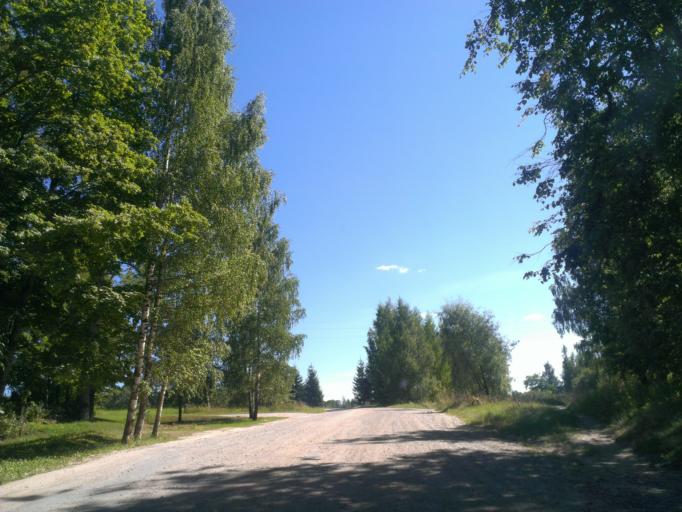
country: LV
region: Malpils
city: Malpils
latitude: 57.0070
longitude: 24.9680
